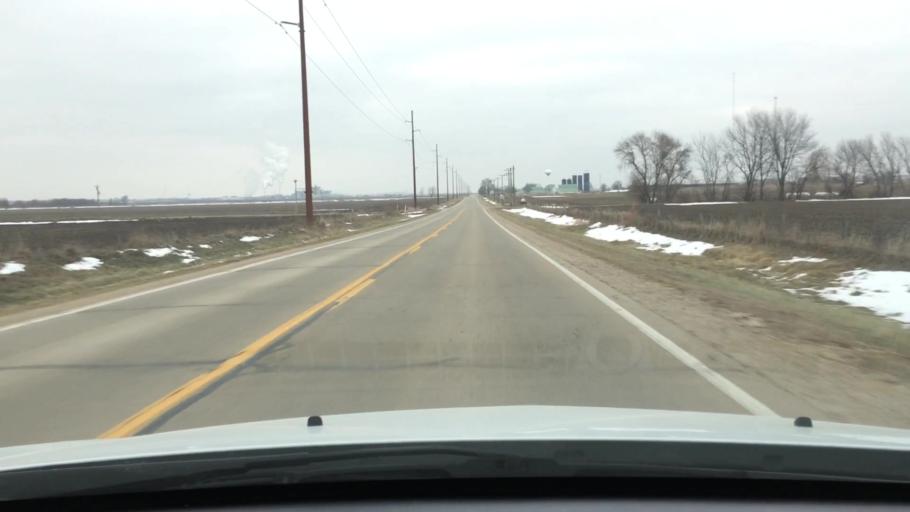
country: US
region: Illinois
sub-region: Ogle County
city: Rochelle
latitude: 41.8605
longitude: -89.0249
